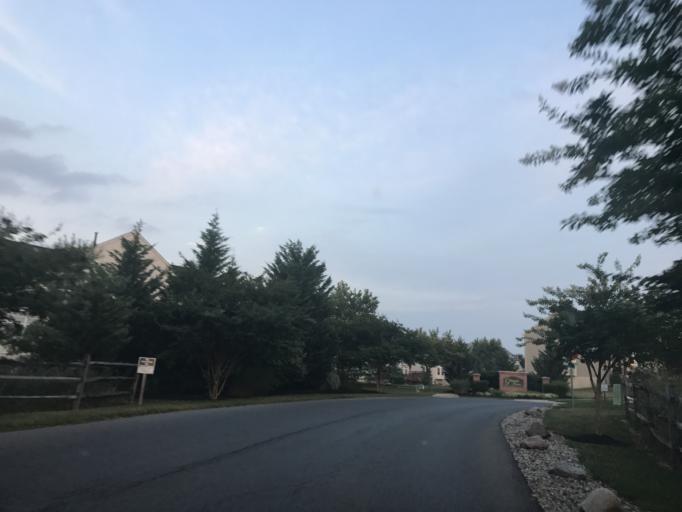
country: US
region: Maryland
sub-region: Baltimore County
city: White Marsh
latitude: 39.4071
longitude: -76.4330
